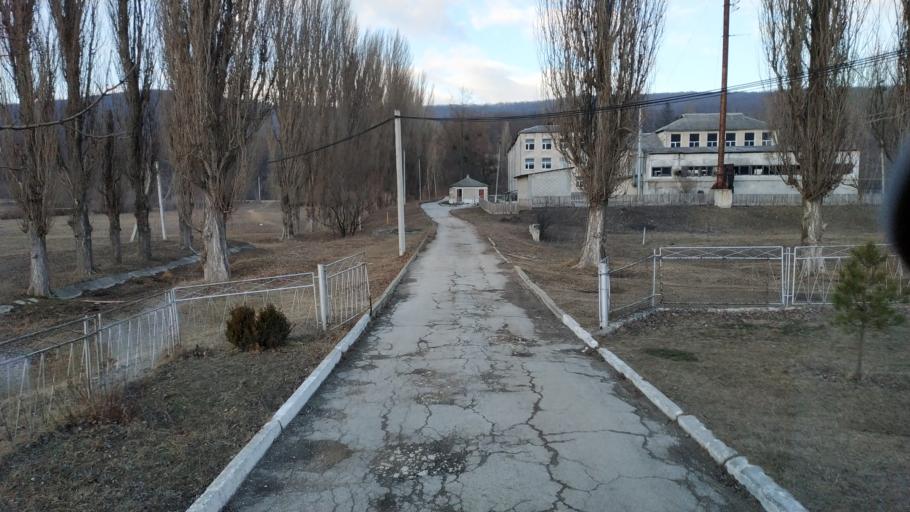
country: MD
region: Calarasi
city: Calarasi
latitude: 47.3289
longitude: 28.2216
